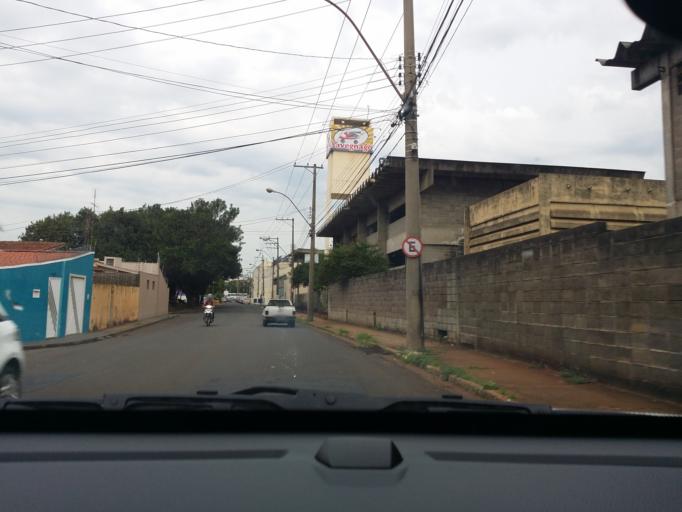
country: BR
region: Sao Paulo
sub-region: Sao Carlos
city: Sao Carlos
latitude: -22.0306
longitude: -47.8925
